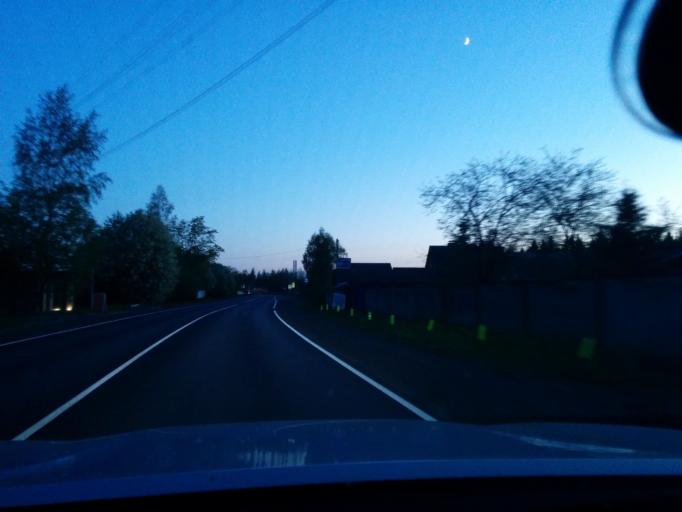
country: RU
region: Leningrad
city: Verkhniye Osel'ki
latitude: 60.1798
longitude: 30.3785
